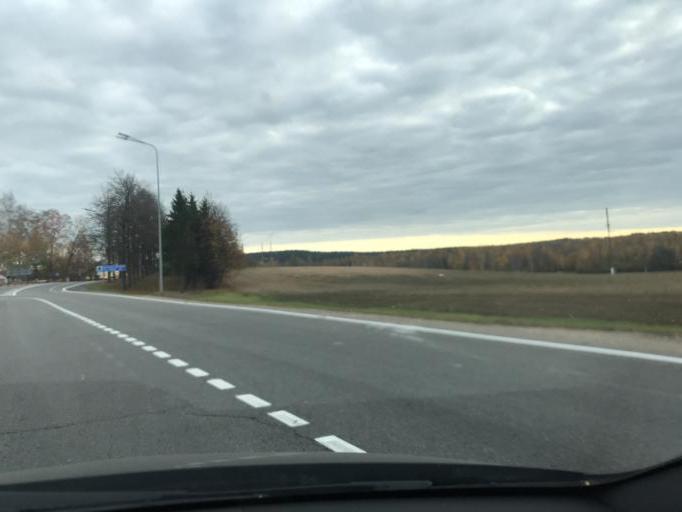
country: BY
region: Minsk
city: Astrashytski Haradok
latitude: 54.0545
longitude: 27.6906
